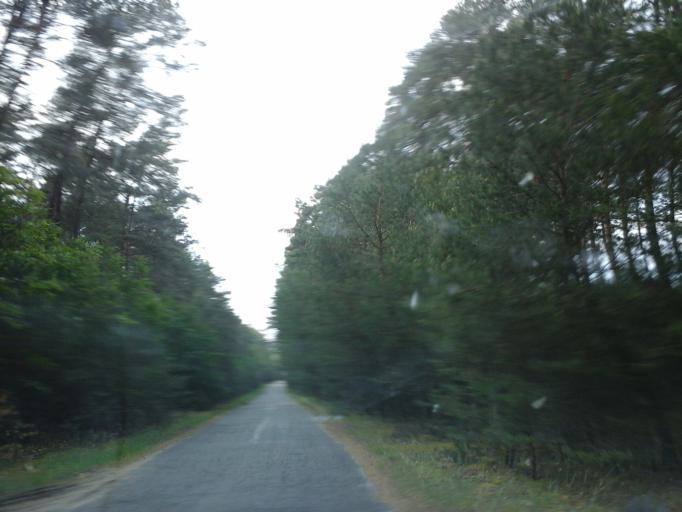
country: PL
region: West Pomeranian Voivodeship
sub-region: Powiat drawski
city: Kalisz Pomorski
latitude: 53.2053
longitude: 15.9432
